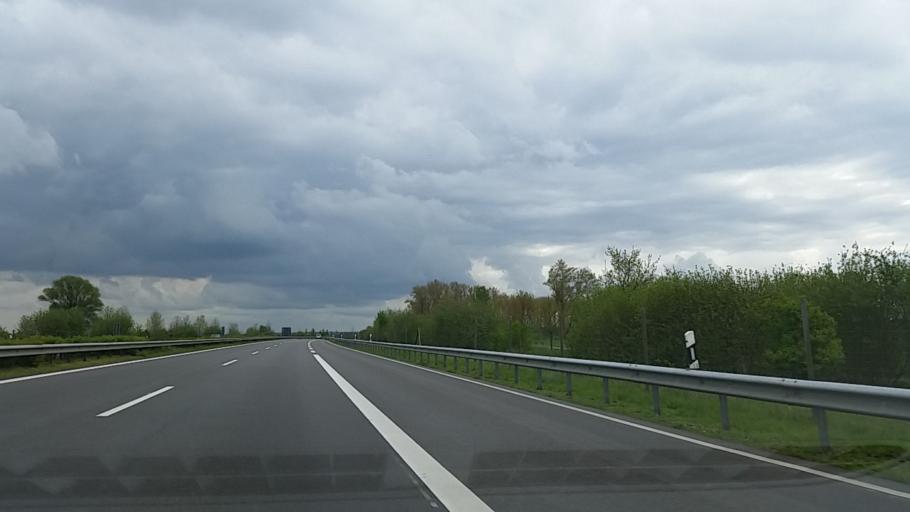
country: DE
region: Lower Saxony
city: Dollern
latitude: 53.5429
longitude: 9.5721
